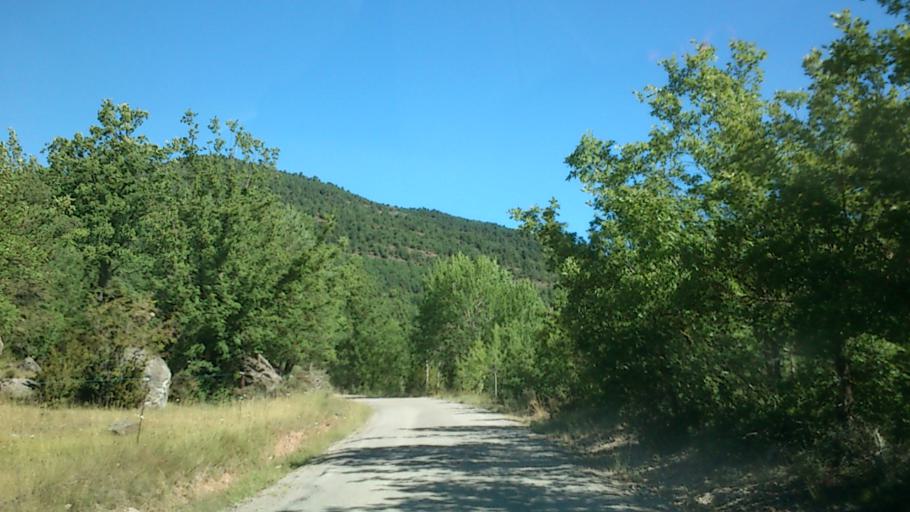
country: ES
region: Aragon
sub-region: Provincia de Huesca
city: Yebra de Basa
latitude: 42.3274
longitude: -0.2567
